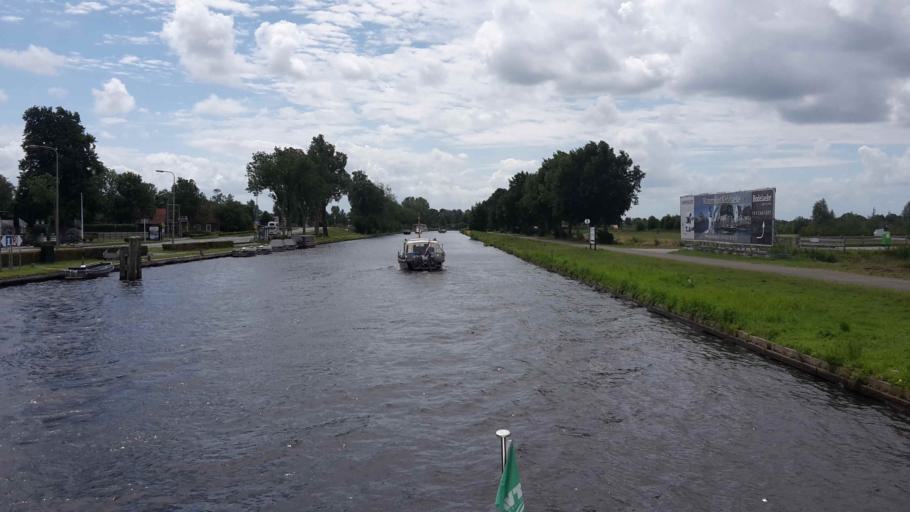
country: NL
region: Overijssel
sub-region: Gemeente Steenwijkerland
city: Giethoorn
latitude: 52.7168
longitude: 6.0767
